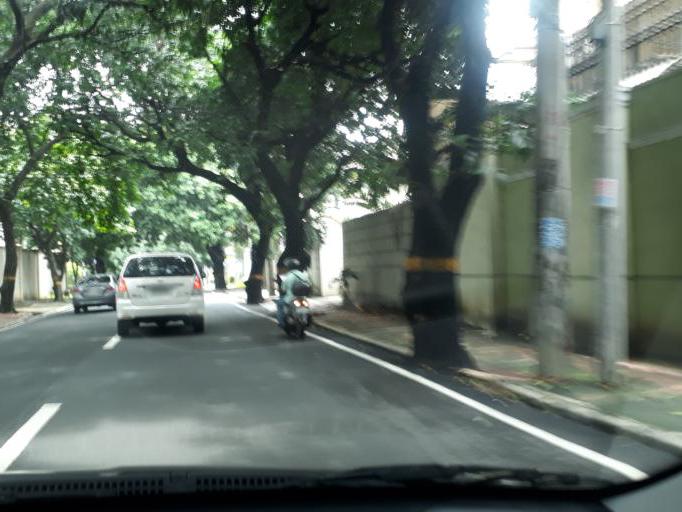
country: PH
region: Metro Manila
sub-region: San Juan
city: San Juan
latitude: 14.6208
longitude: 121.0303
